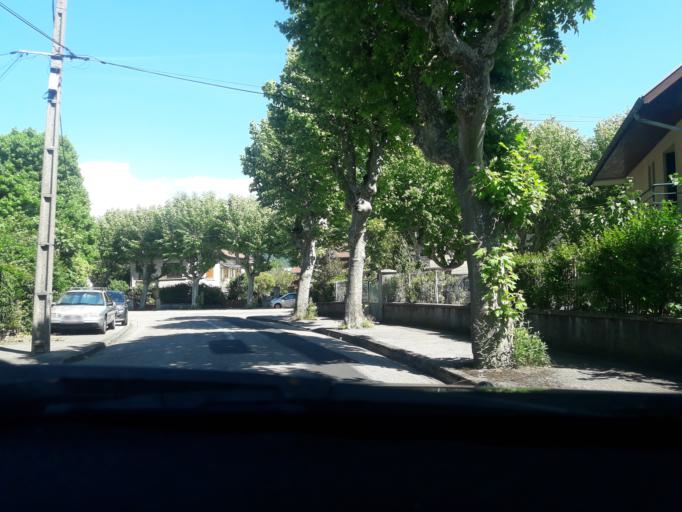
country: FR
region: Rhone-Alpes
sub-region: Departement de l'Isere
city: Eybens
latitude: 45.1664
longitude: 5.7396
